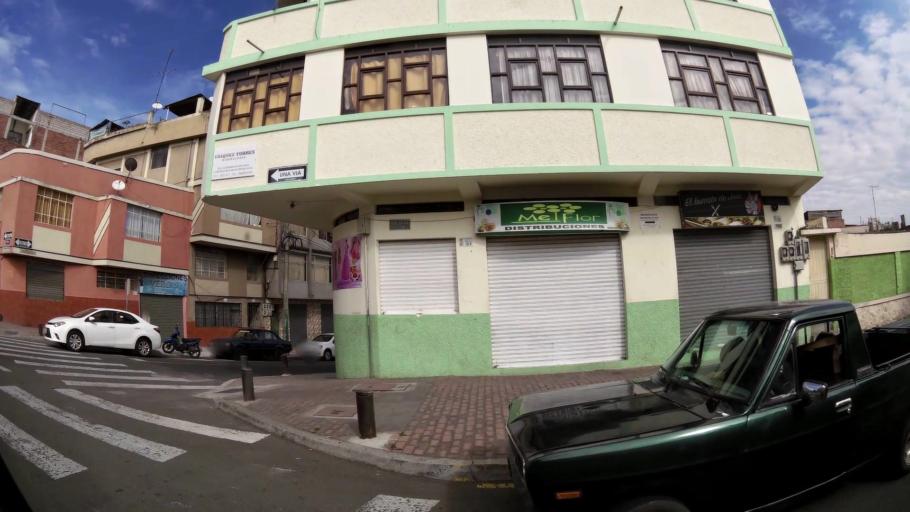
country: EC
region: Tungurahua
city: Ambato
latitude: -1.2470
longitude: -78.6350
